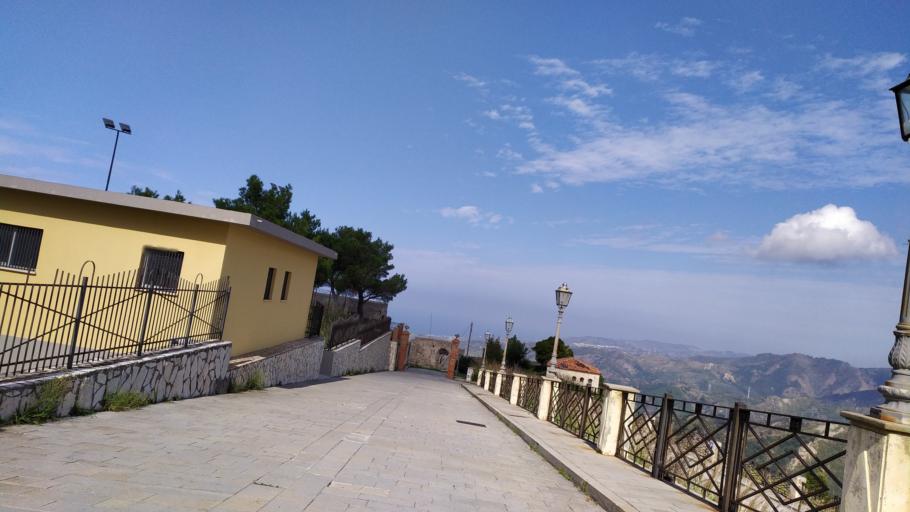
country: IT
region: Sicily
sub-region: Messina
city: Rometta
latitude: 38.1730
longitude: 15.4162
